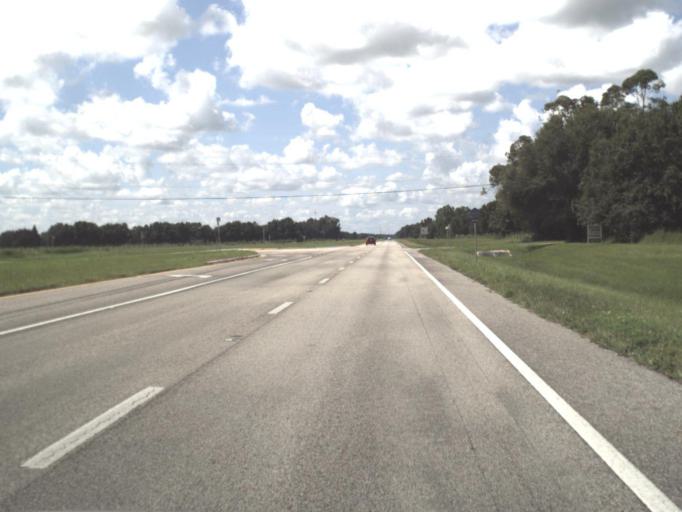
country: US
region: Florida
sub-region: DeSoto County
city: Arcadia
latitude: 27.2830
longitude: -81.8306
